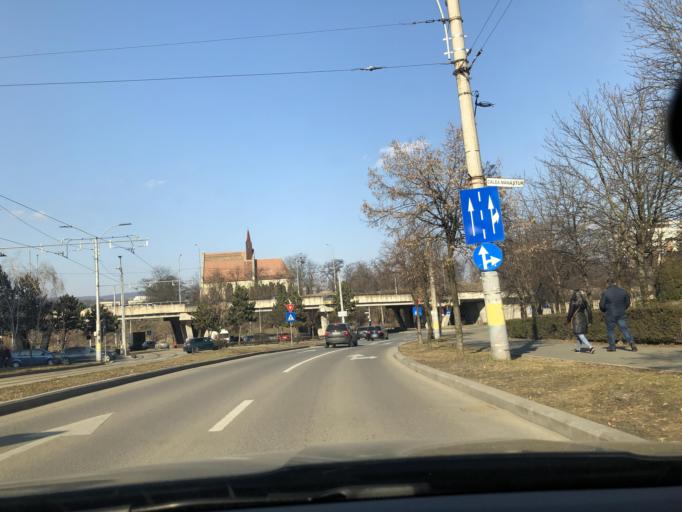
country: RO
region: Cluj
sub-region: Municipiul Cluj-Napoca
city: Cluj-Napoca
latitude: 46.7590
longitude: 23.5575
